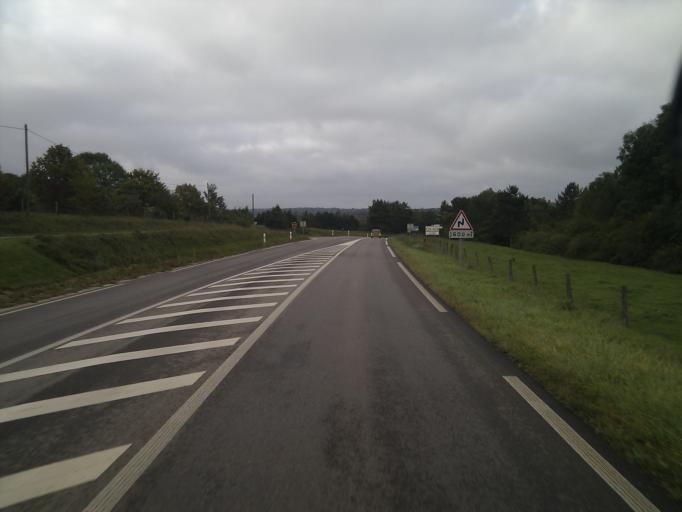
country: FR
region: Lorraine
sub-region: Departement des Vosges
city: Neufchateau
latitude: 48.4078
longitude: 5.7425
